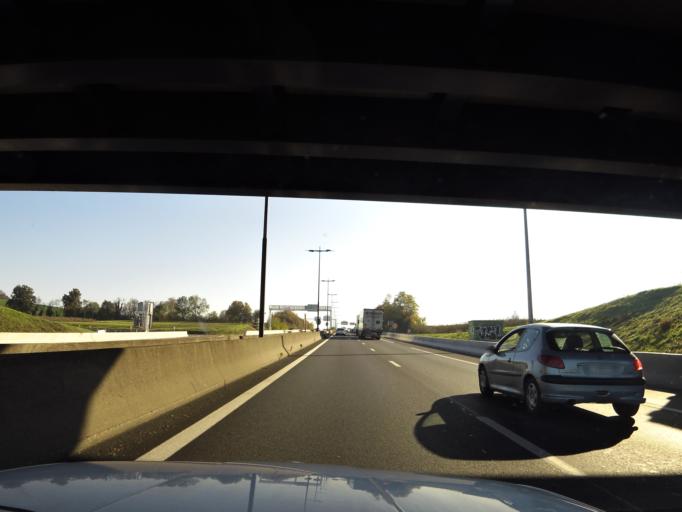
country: FR
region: Rhone-Alpes
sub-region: Departement du Rhone
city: Decines-Charpieu
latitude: 45.7587
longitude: 4.9853
